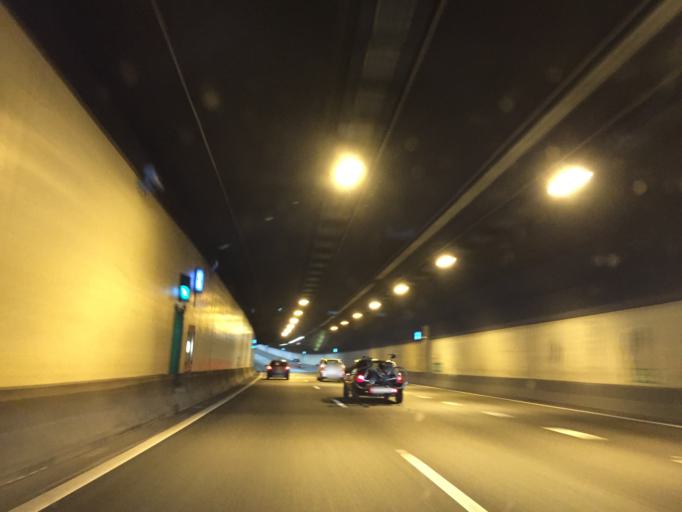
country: NL
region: South Holland
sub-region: Gemeente Spijkenisse
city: Spijkenisse
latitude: 51.8701
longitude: 4.3281
